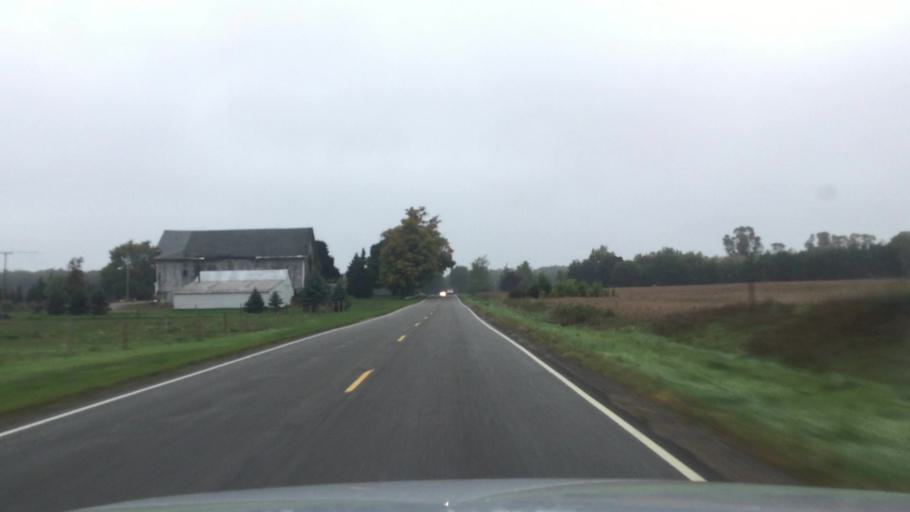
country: US
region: Michigan
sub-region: Shiawassee County
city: Corunna
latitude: 42.9242
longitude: -84.1242
